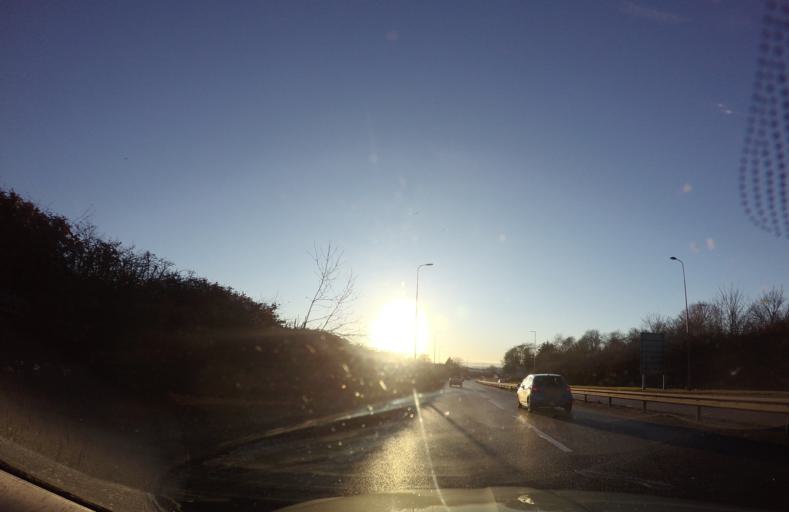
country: GB
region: Scotland
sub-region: Angus
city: Muirhead
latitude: 56.4792
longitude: -3.0262
